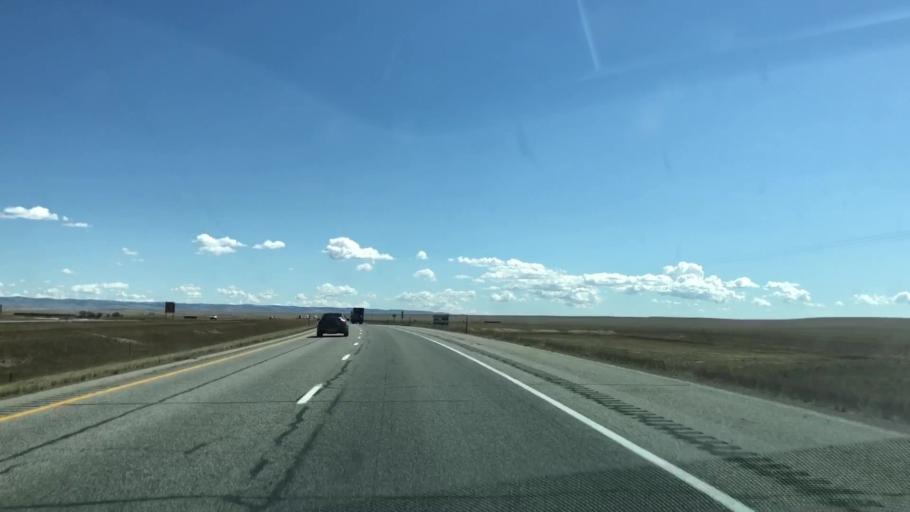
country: US
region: Wyoming
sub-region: Albany County
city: Laramie
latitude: 41.3802
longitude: -105.8103
